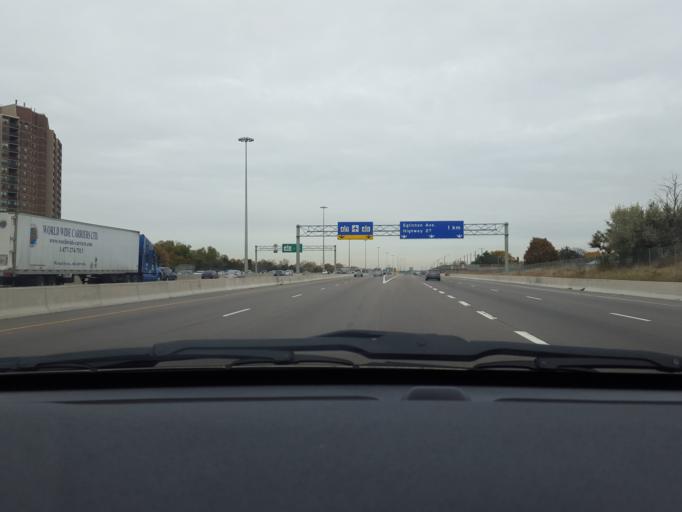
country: CA
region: Ontario
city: Etobicoke
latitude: 43.6552
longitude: -79.5675
